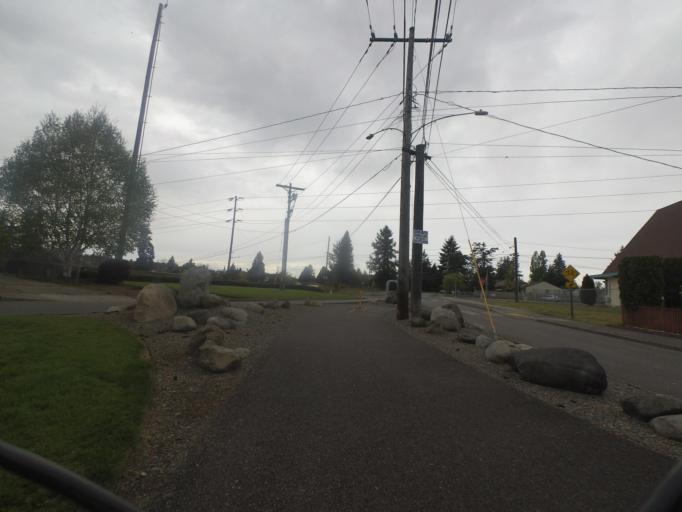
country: US
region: Washington
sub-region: Pierce County
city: Lakewood
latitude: 47.1969
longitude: -122.4760
